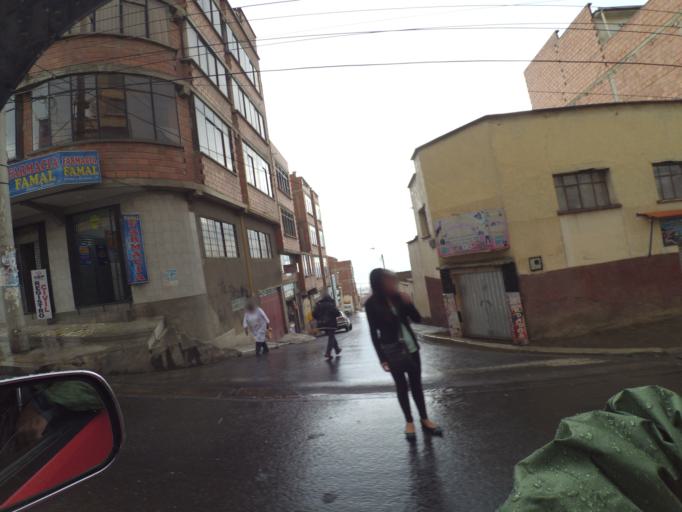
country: BO
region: La Paz
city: La Paz
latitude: -16.4890
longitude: -68.1676
